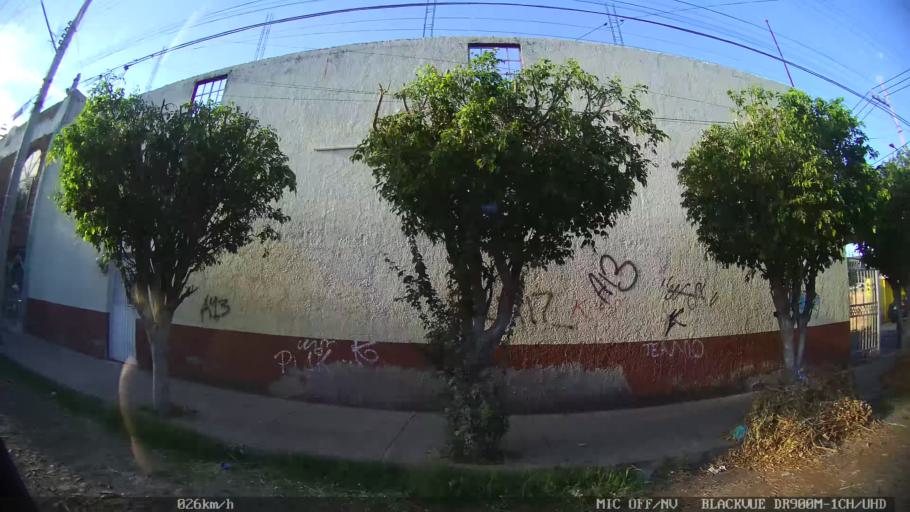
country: MX
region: Jalisco
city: Tlaquepaque
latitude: 20.7051
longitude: -103.2979
